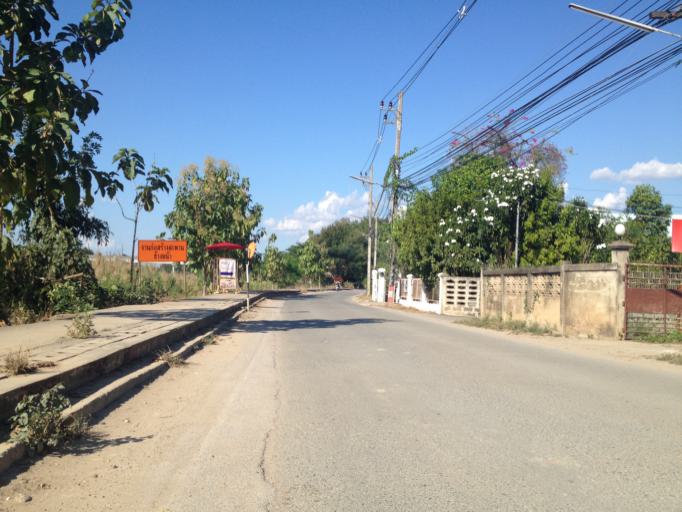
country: TH
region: Chiang Mai
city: Saraphi
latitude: 18.7164
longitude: 98.9875
